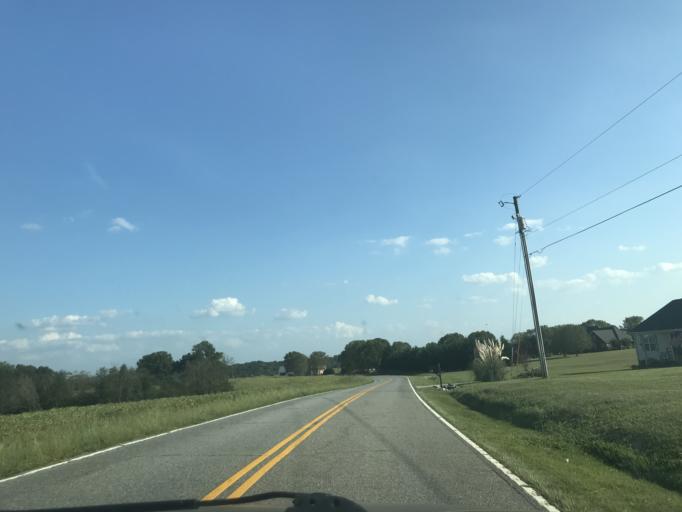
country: US
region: South Carolina
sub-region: Cherokee County
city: Gaffney
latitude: 35.1281
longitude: -81.6890
